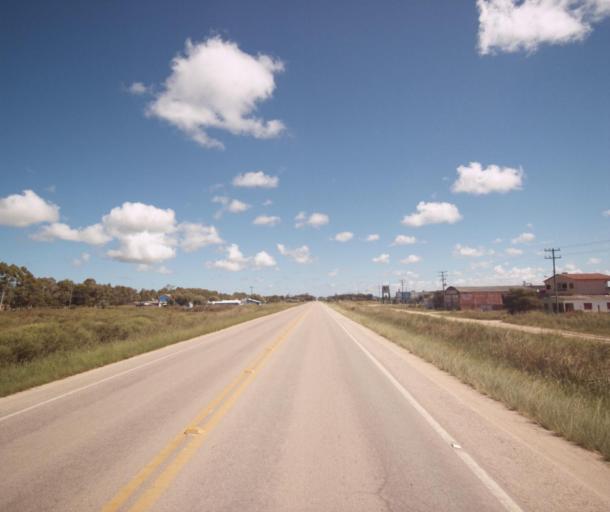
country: BR
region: Rio Grande do Sul
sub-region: Santa Vitoria Do Palmar
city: Santa Vitoria do Palmar
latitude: -33.5279
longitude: -53.3428
